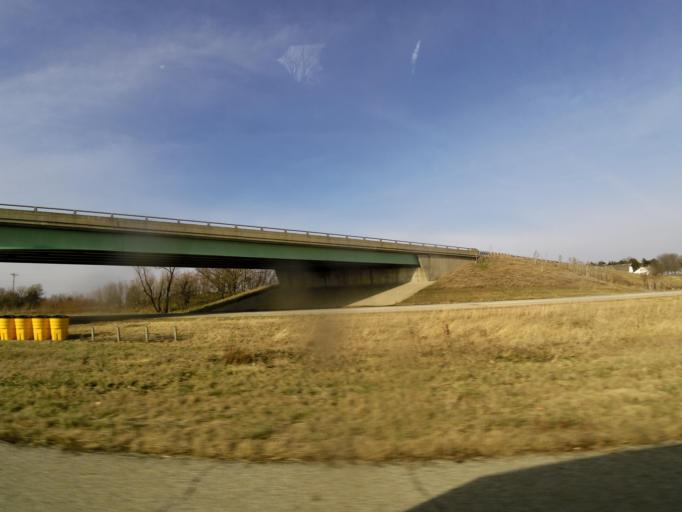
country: US
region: Illinois
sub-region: Macon County
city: Harristown
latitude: 39.8757
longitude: -89.0286
